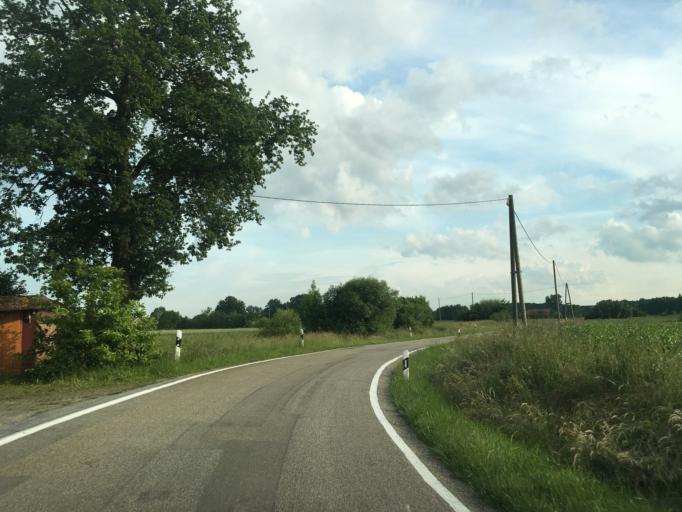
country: DE
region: North Rhine-Westphalia
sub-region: Regierungsbezirk Munster
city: Altenberge
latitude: 52.0026
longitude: 7.4798
